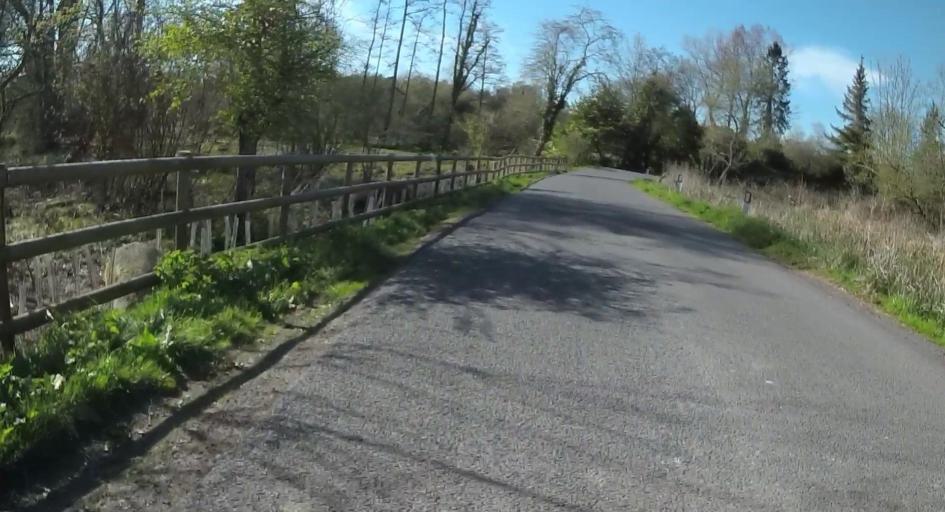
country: GB
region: England
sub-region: Hampshire
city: Abbotts Ann
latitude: 51.1303
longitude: -1.4853
